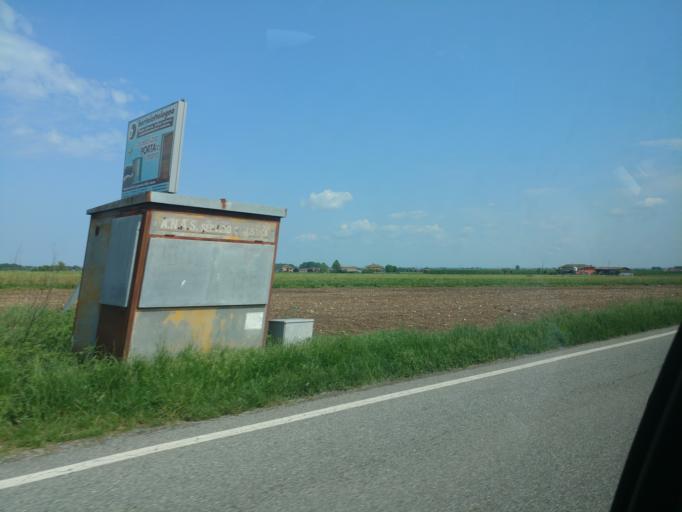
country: IT
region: Piedmont
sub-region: Provincia di Torino
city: Cavour
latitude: 44.7656
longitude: 7.3952
